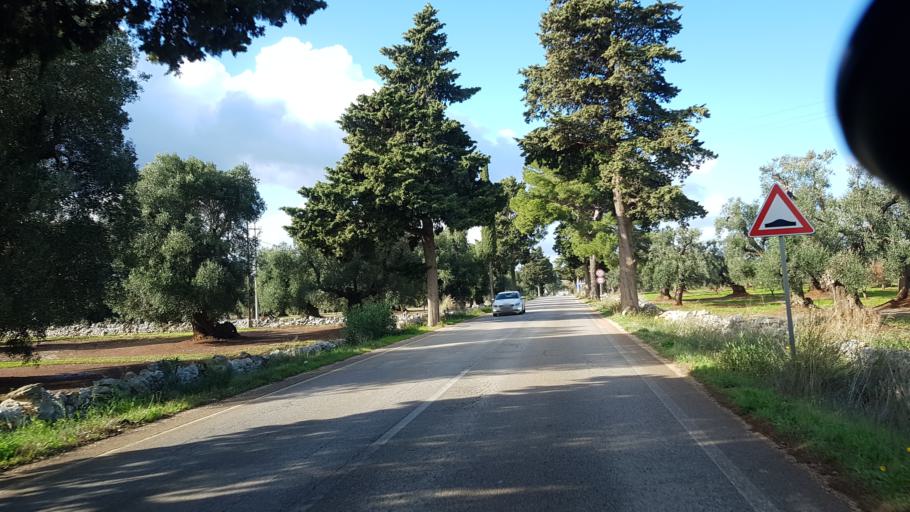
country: IT
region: Apulia
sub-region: Provincia di Brindisi
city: Montalbano
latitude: 40.7959
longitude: 17.4506
